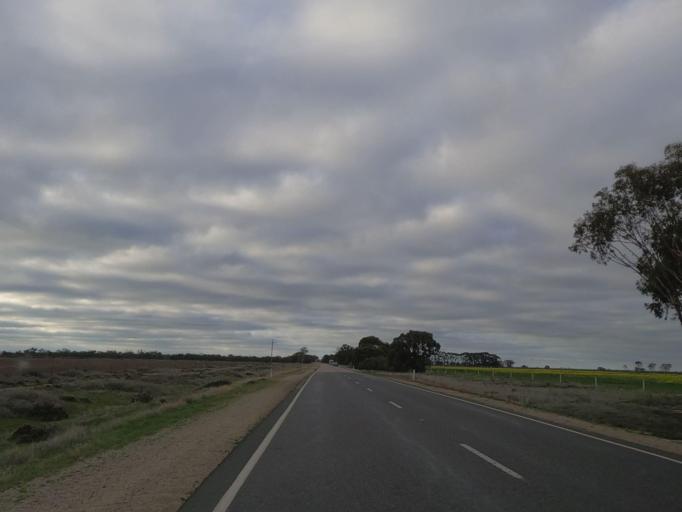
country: AU
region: Victoria
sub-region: Swan Hill
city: Swan Hill
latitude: -35.8272
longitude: 143.9461
